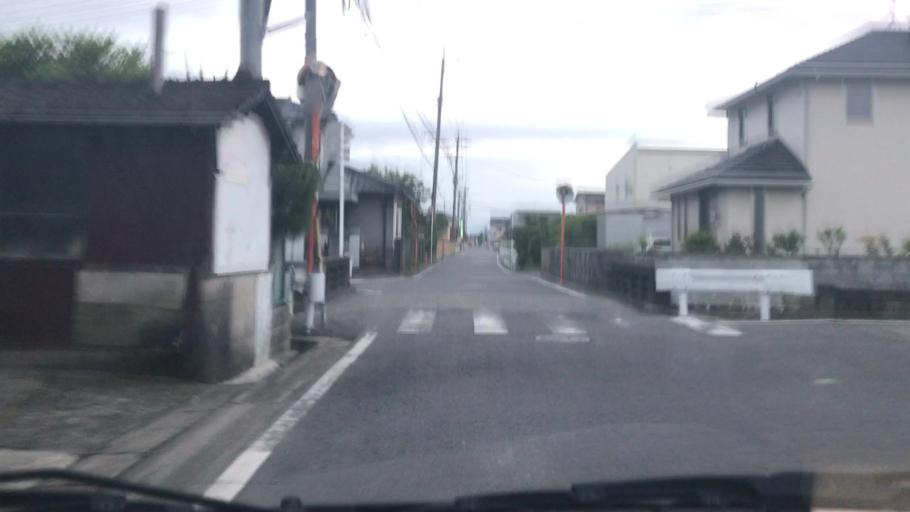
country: JP
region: Saga Prefecture
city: Saga-shi
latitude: 33.2339
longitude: 130.3017
